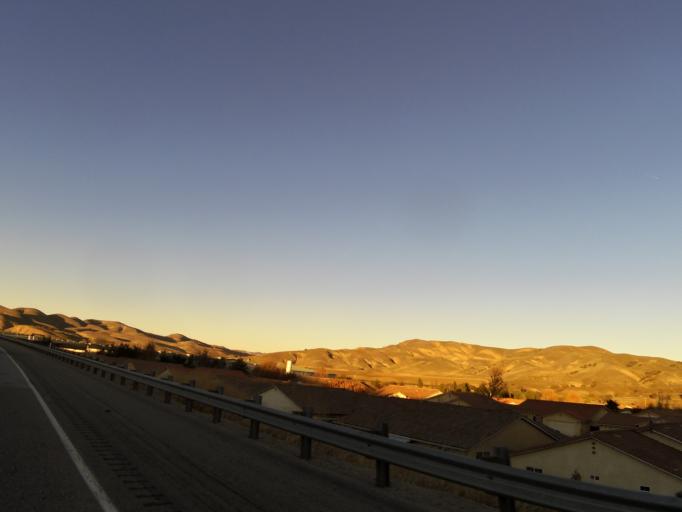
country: US
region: California
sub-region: San Luis Obispo County
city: San Miguel
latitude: 35.7603
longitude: -120.6987
